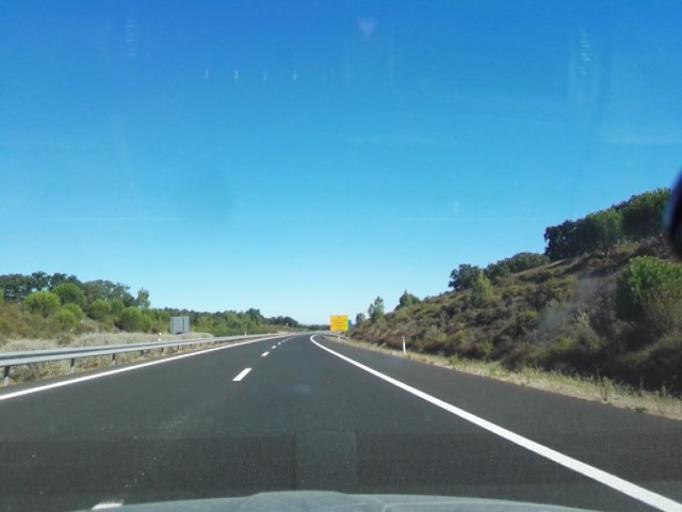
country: PT
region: Santarem
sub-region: Benavente
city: Poceirao
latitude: 38.8816
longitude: -8.7941
